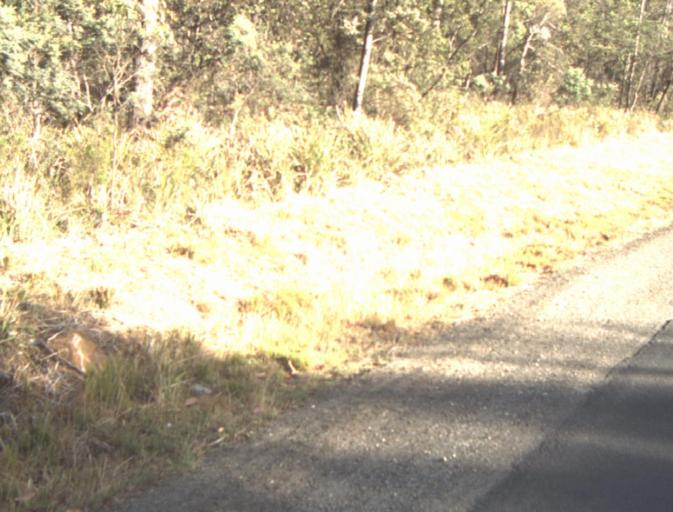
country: AU
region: Tasmania
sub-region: Launceston
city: Mayfield
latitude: -41.3353
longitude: 147.1781
